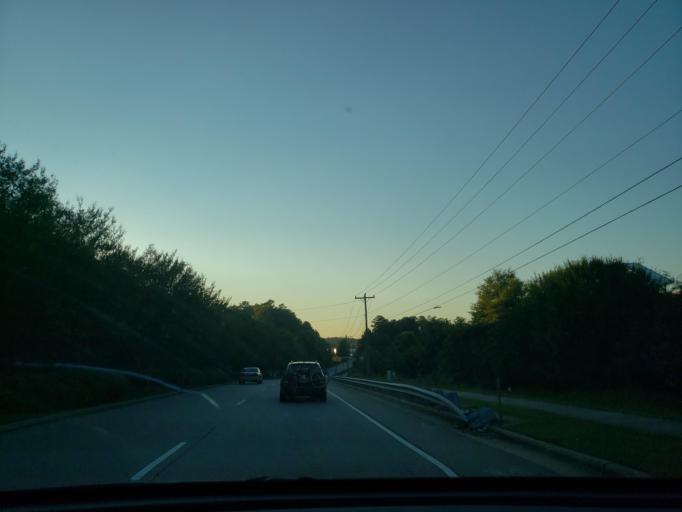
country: US
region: North Carolina
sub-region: Durham County
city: Durham
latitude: 35.9400
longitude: -78.9083
